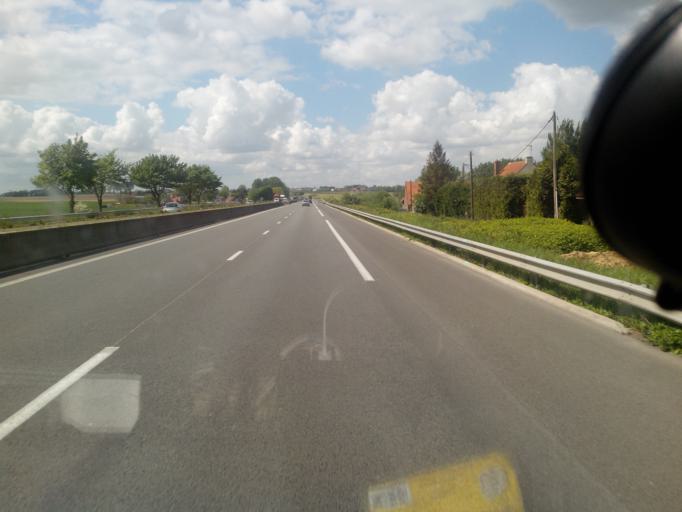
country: FR
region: Nord-Pas-de-Calais
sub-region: Departement du Nord
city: Meteren
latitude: 50.7411
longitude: 2.6815
